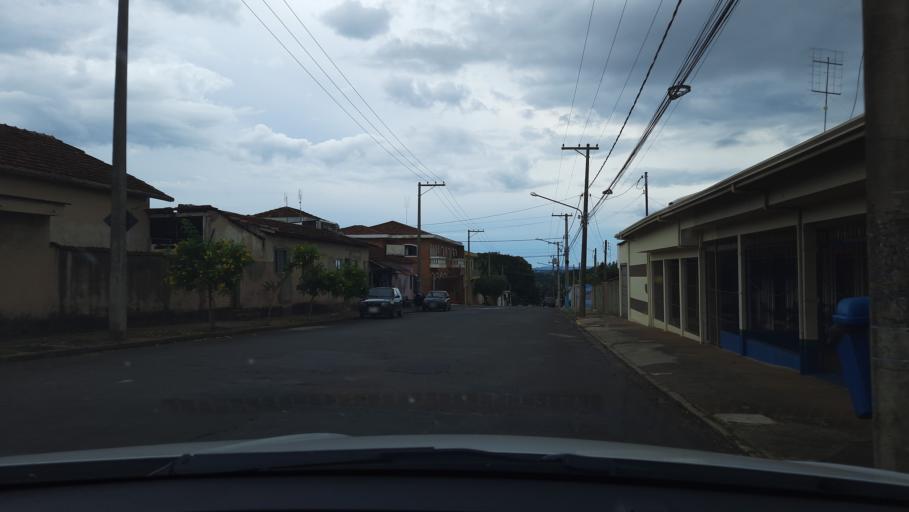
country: BR
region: Sao Paulo
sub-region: Casa Branca
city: Casa Branca
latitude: -21.7782
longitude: -47.0765
